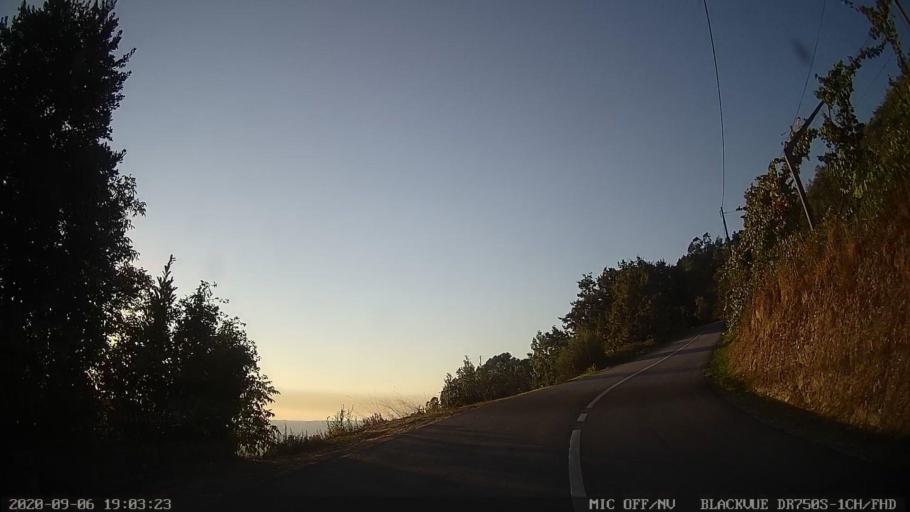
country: PT
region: Porto
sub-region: Baiao
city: Baiao
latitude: 41.2319
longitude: -7.9968
